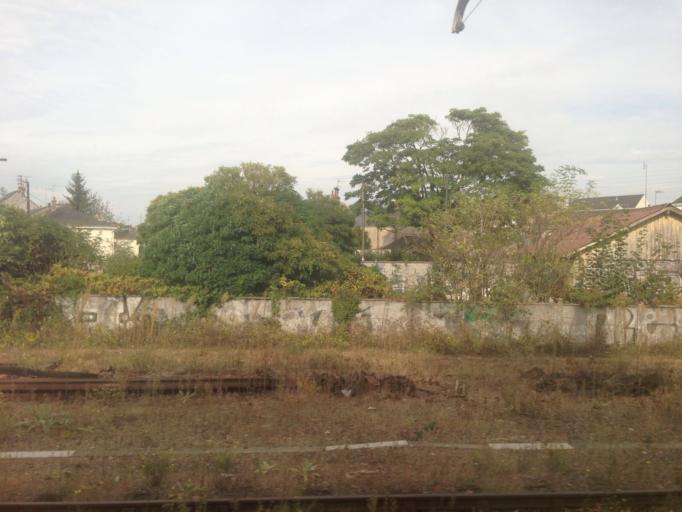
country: FR
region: Centre
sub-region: Departement d'Indre-et-Loire
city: Tours
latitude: 47.3824
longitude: 0.7036
